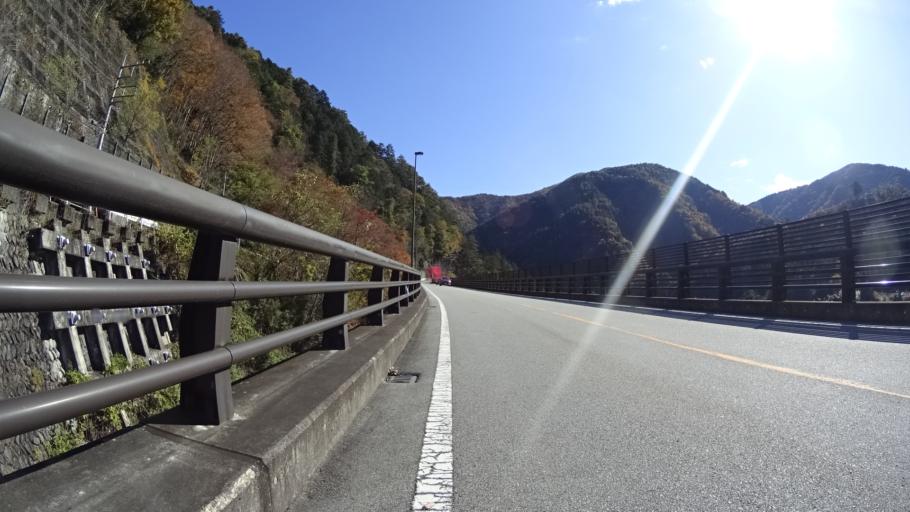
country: JP
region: Yamanashi
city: Otsuki
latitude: 35.7894
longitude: 138.9254
